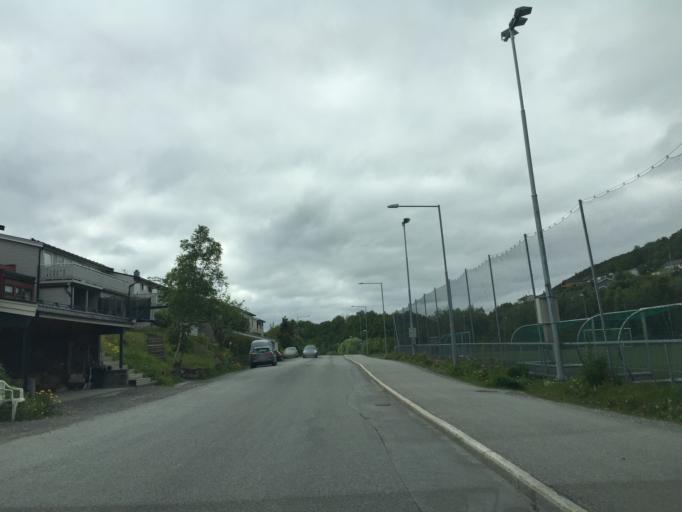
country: NO
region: Nordland
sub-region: Bodo
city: Lopsmarka
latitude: 67.2839
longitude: 14.5329
